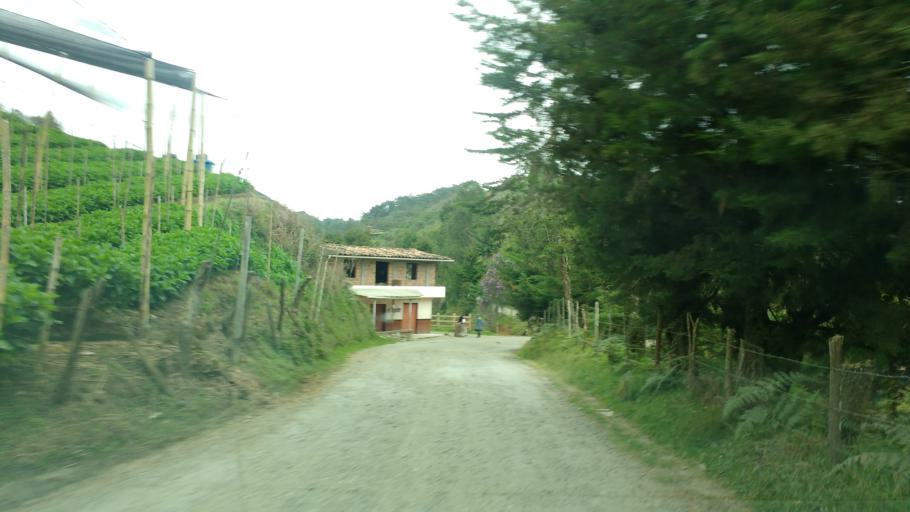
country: CO
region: Antioquia
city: Concepcion
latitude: 6.3432
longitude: -75.2690
